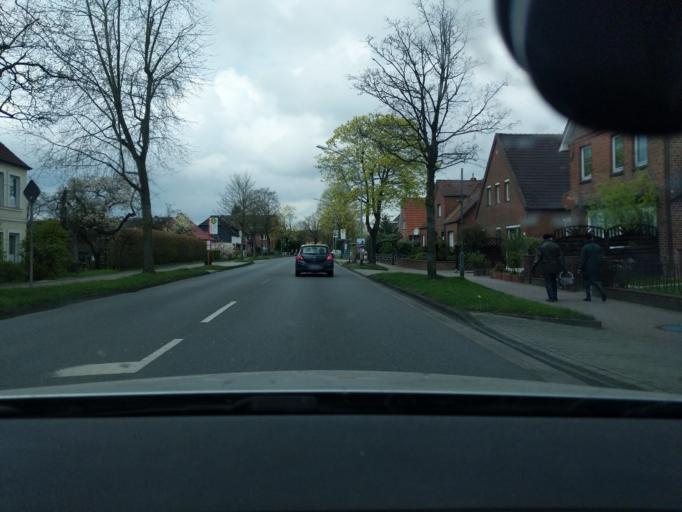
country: DE
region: Lower Saxony
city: Stade
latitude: 53.5862
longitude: 9.4922
